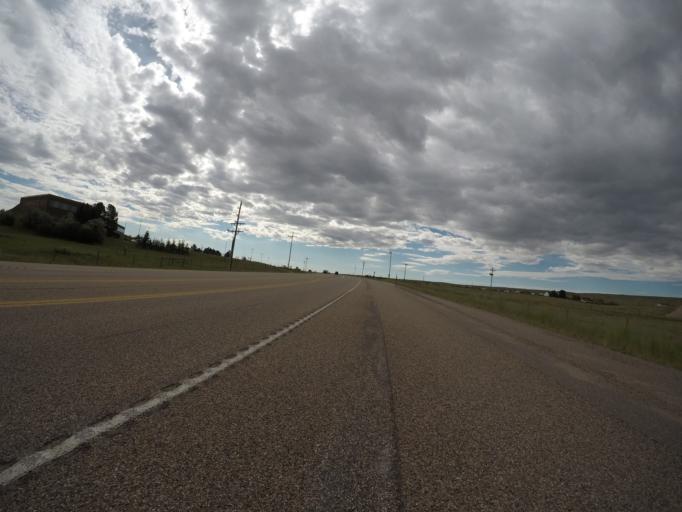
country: US
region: Wyoming
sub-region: Laramie County
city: Cheyenne
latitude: 41.1580
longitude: -105.0776
